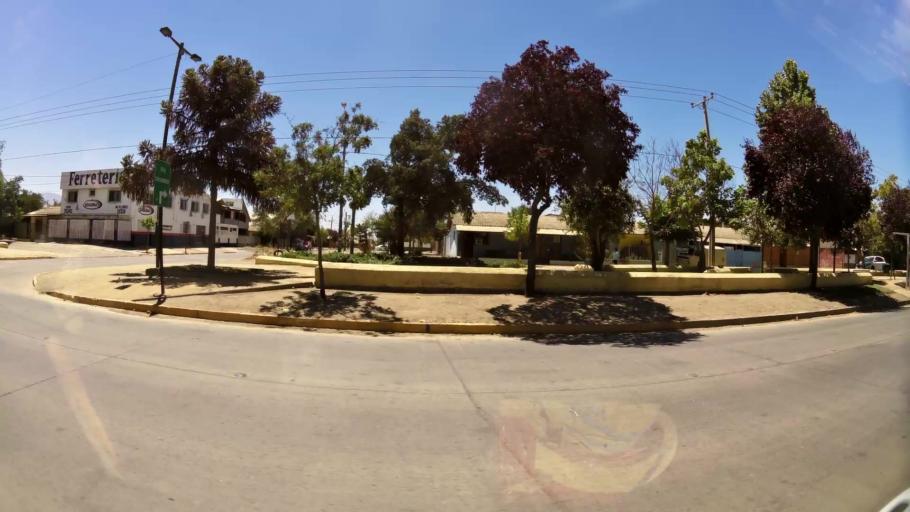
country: CL
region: O'Higgins
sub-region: Provincia de Cachapoal
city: Rancagua
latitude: -34.1602
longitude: -70.7156
